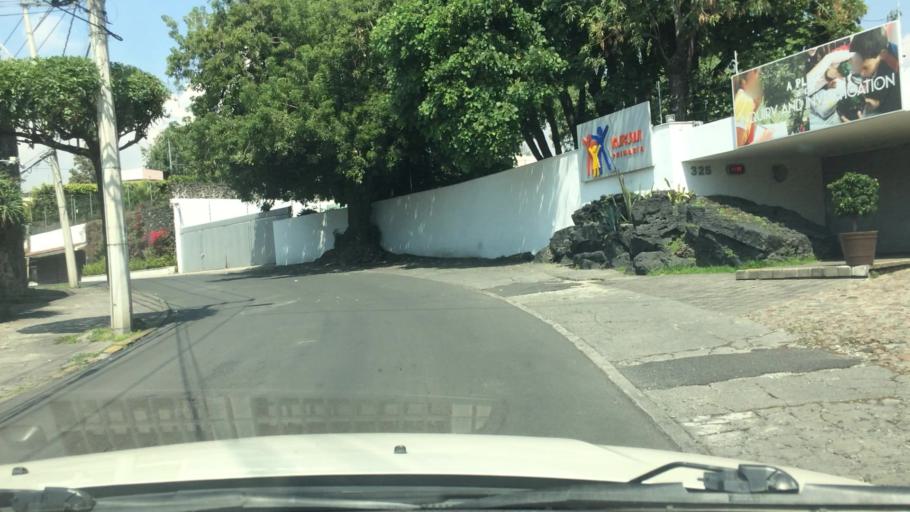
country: MX
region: Mexico City
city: Magdalena Contreras
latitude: 19.3259
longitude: -99.2097
